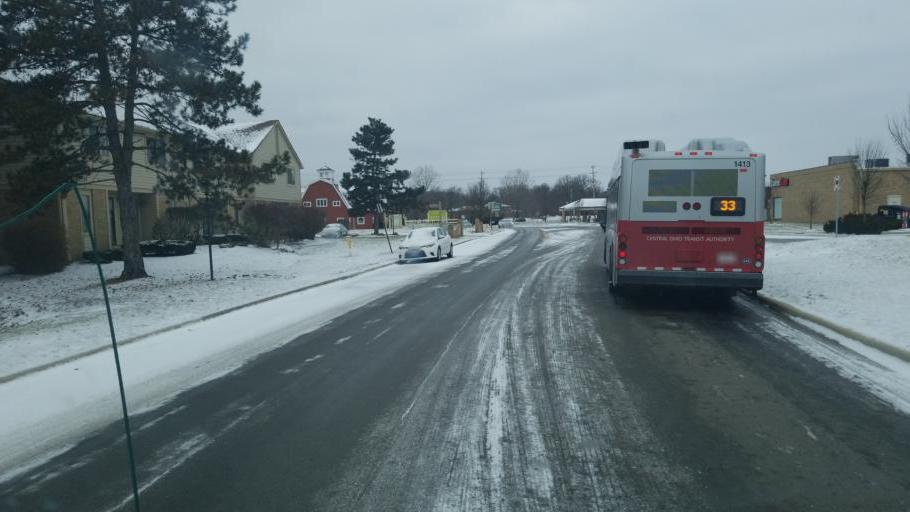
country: US
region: Ohio
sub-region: Franklin County
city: Dublin
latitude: 40.1214
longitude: -83.0882
